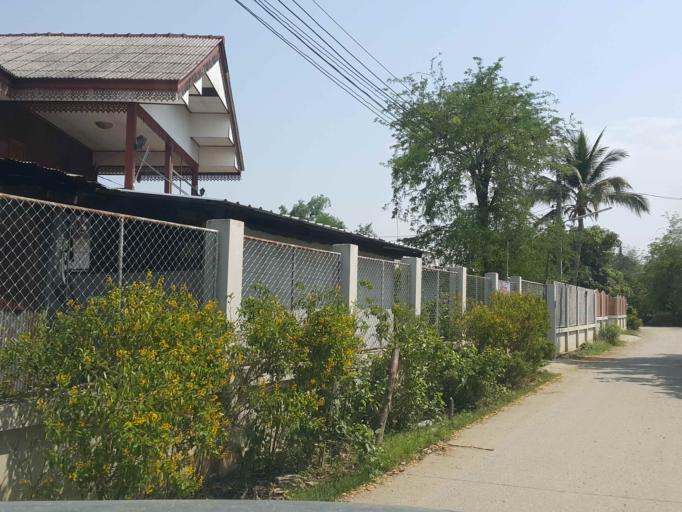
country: TH
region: Chiang Mai
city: San Kamphaeng
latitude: 18.7845
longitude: 99.1126
